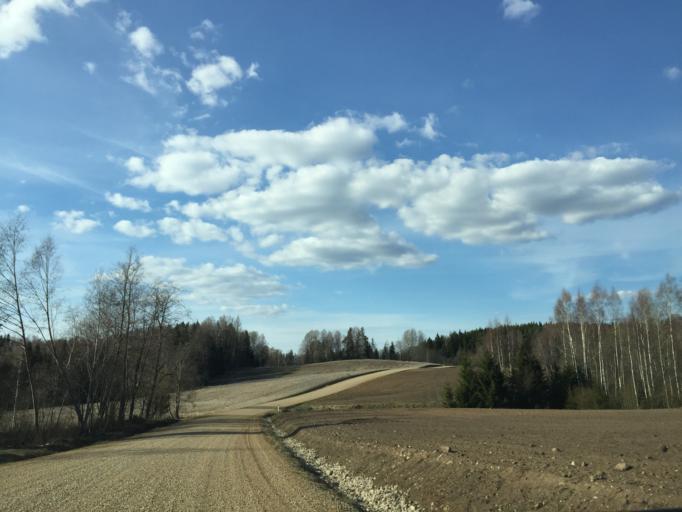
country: EE
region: Tartu
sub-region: Elva linn
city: Elva
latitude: 58.0949
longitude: 26.5091
